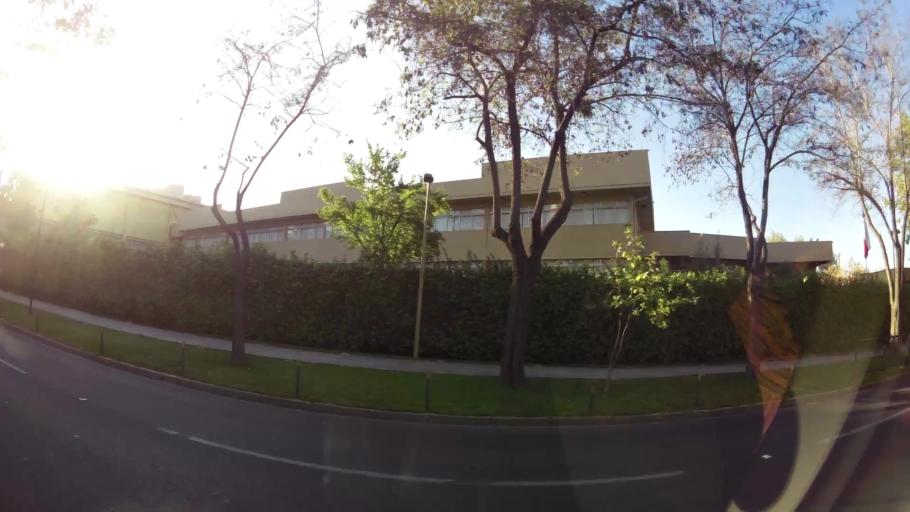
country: CL
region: Santiago Metropolitan
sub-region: Provincia de Santiago
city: Villa Presidente Frei, Nunoa, Santiago, Chile
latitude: -33.4004
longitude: -70.5665
